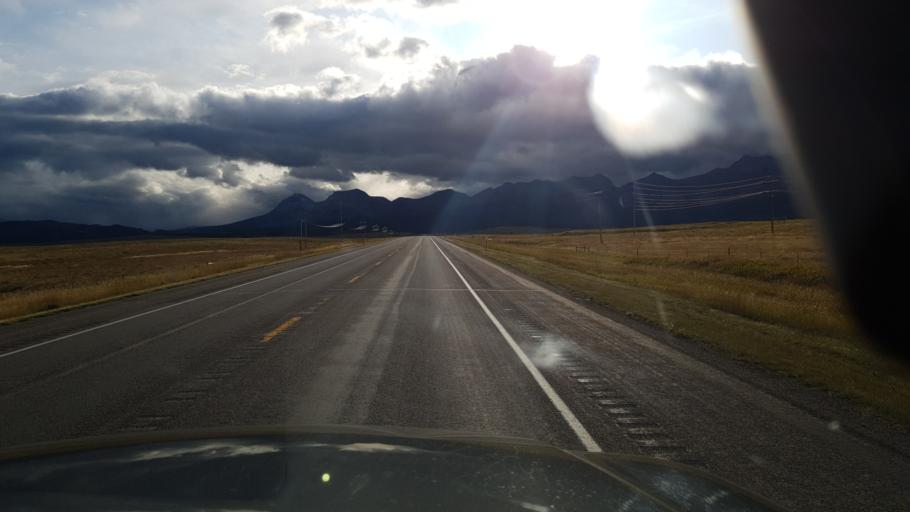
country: US
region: Montana
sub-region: Glacier County
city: South Browning
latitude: 48.4621
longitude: -113.1684
